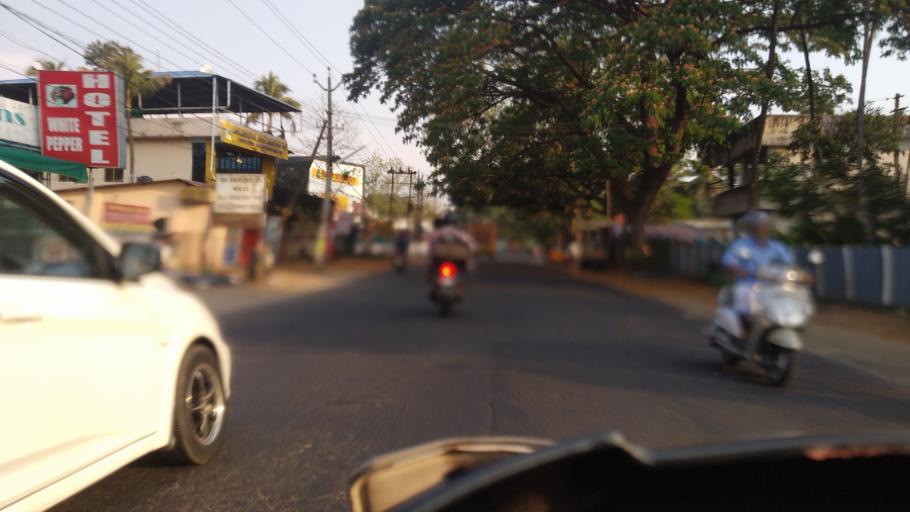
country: IN
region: Kerala
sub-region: Thrissur District
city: Thanniyam
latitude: 10.3966
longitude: 76.1156
